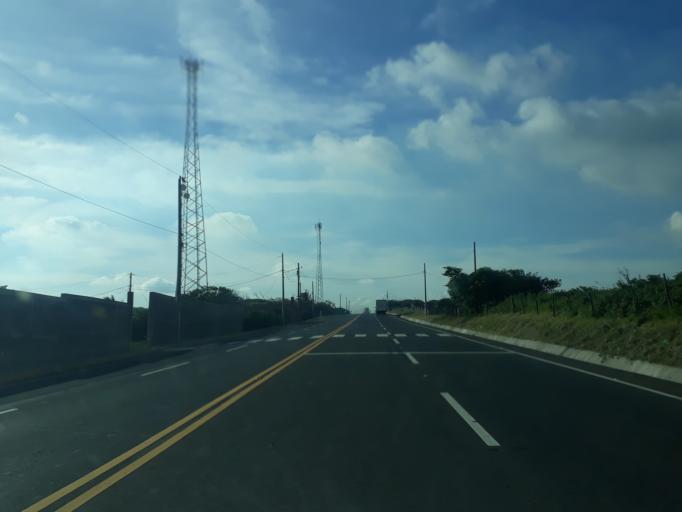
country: NI
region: Managua
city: El Crucero
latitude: 11.9238
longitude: -86.2819
